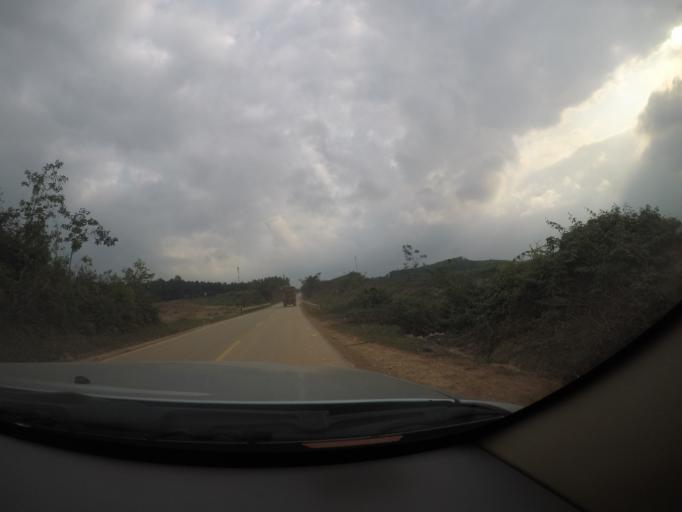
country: VN
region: Quang Tri
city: Ho Xa
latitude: 17.0814
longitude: 106.8618
